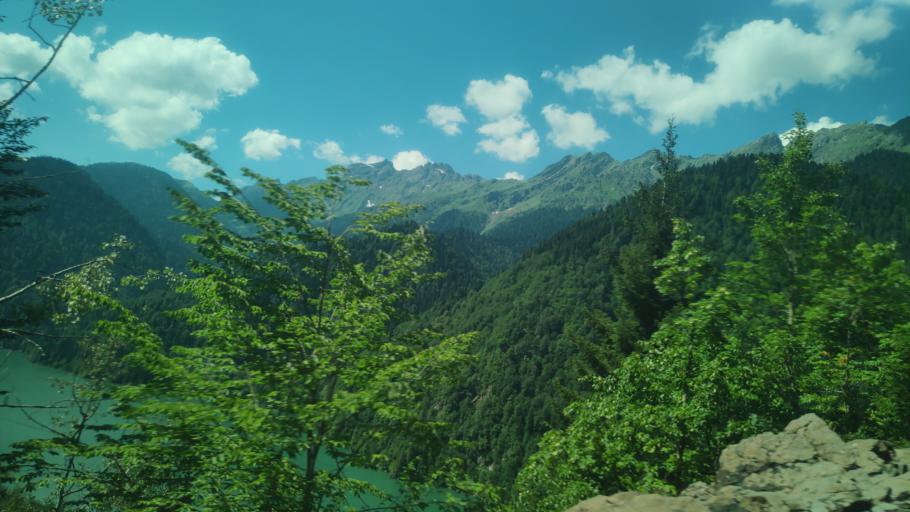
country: GE
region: Abkhazia
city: Gagra
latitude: 43.4783
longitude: 40.5577
